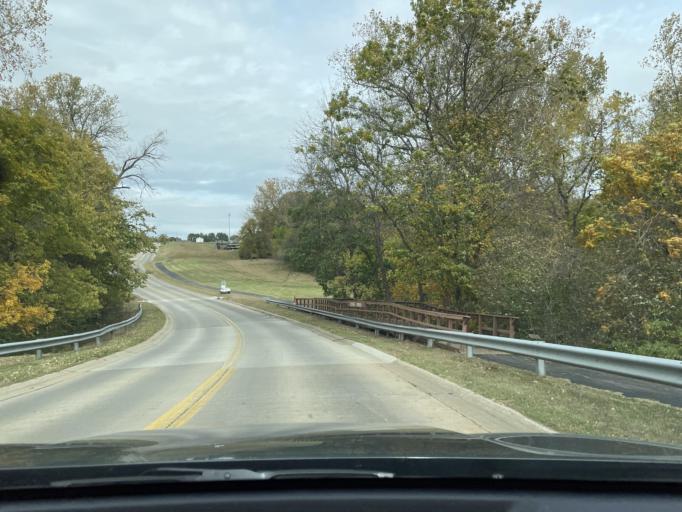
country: US
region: Missouri
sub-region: Buchanan County
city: Saint Joseph
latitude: 39.7644
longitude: -94.7808
